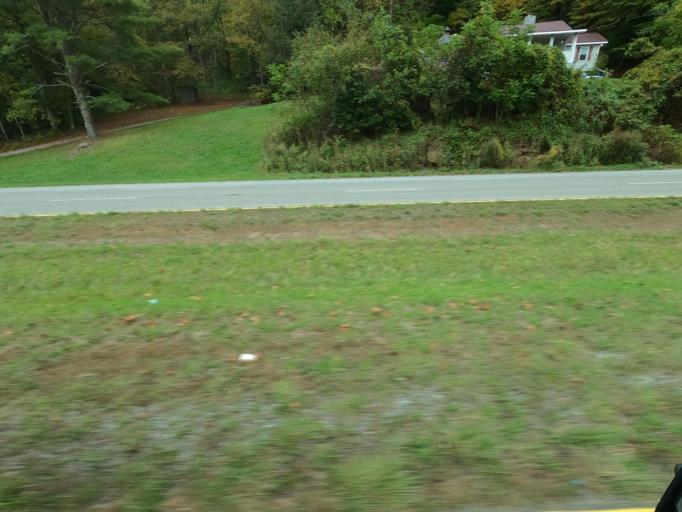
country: US
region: Tennessee
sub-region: Carter County
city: Elizabethton
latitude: 36.2430
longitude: -82.1900
